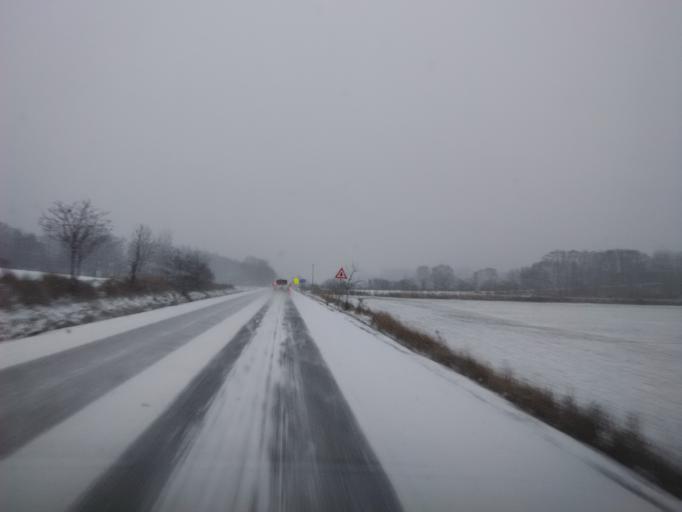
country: CZ
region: Olomoucky
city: Belotin
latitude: 49.5390
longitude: 17.8102
